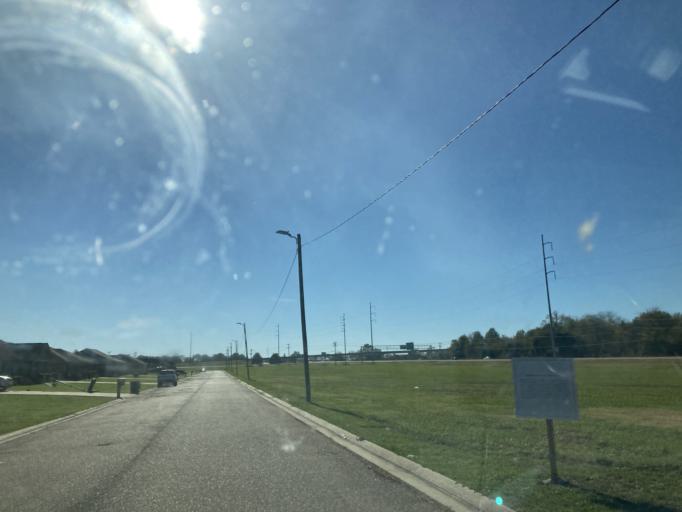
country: US
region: Mississippi
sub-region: Yazoo County
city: Yazoo City
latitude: 32.8594
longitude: -90.4278
